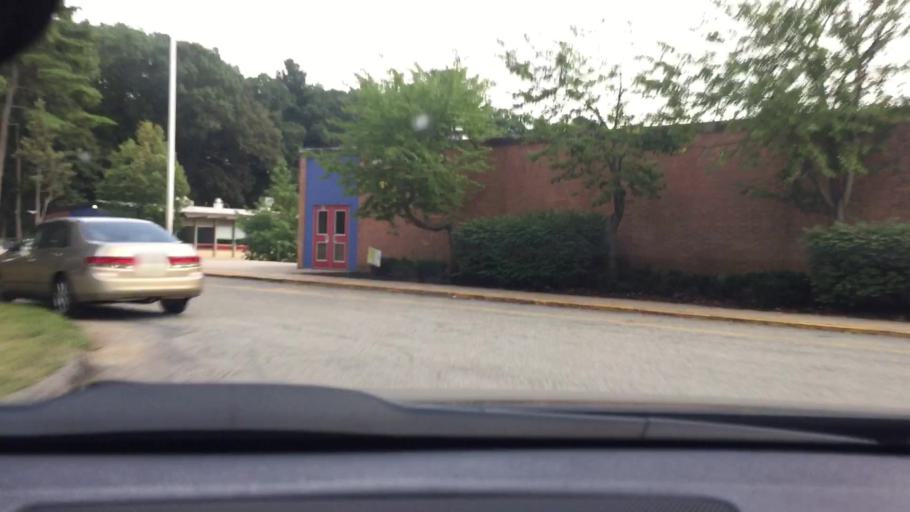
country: US
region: Massachusetts
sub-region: Norfolk County
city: Needham
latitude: 42.2771
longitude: -71.2265
